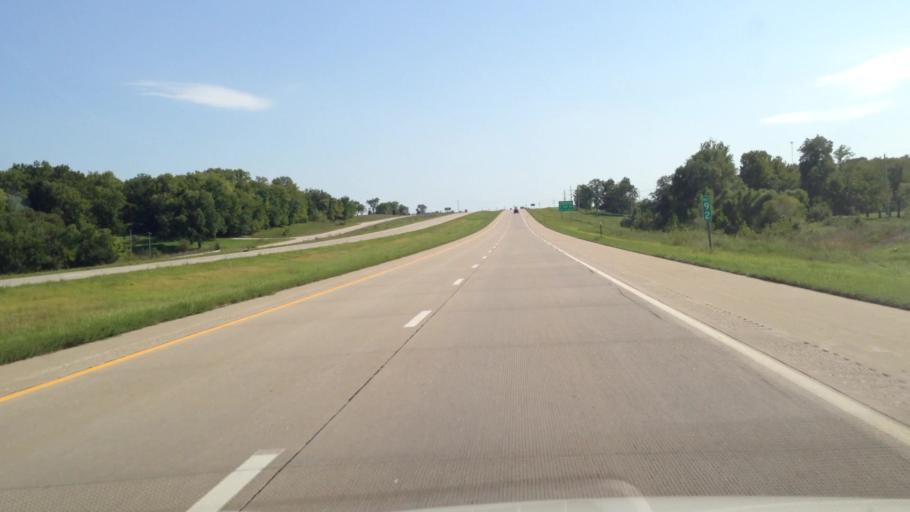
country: US
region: Kansas
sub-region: Linn County
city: Pleasanton
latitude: 38.2035
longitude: -94.7056
